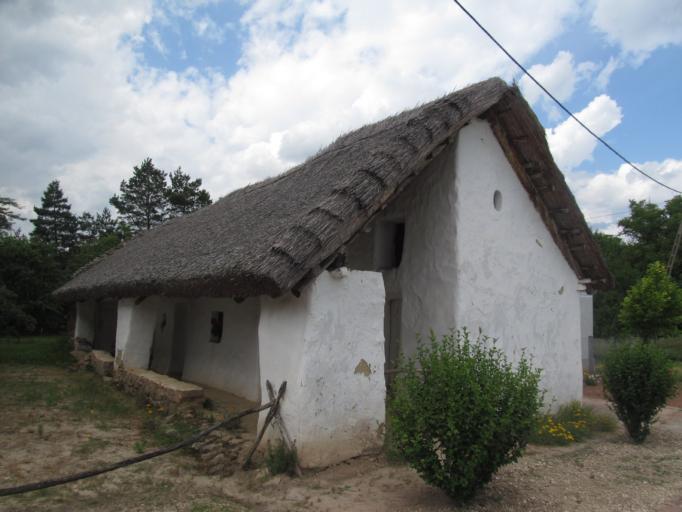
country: HU
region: Veszprem
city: Badacsonytomaj
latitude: 46.8481
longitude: 17.5572
